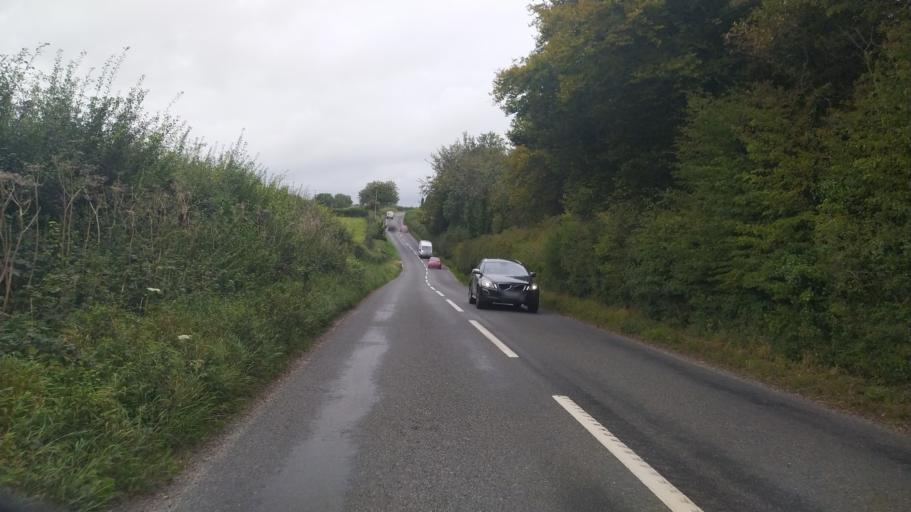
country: GB
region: England
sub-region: Dorset
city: Dorchester
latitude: 50.7682
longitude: -2.3981
